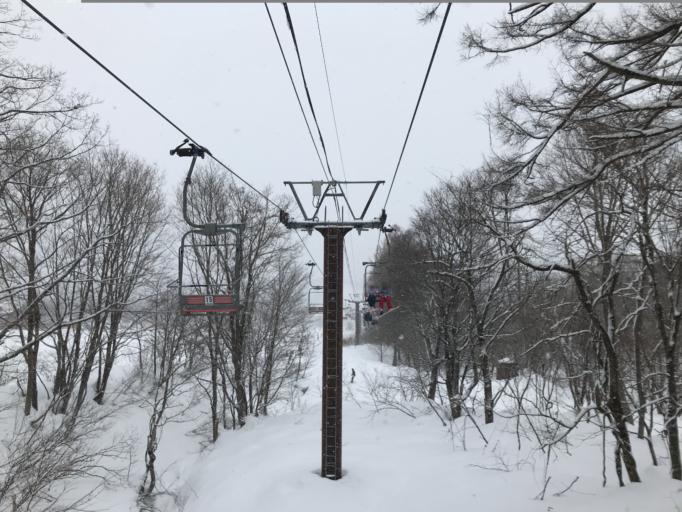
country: JP
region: Nagano
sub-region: Kitaazumi Gun
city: Hakuba
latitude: 36.7540
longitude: 137.8637
